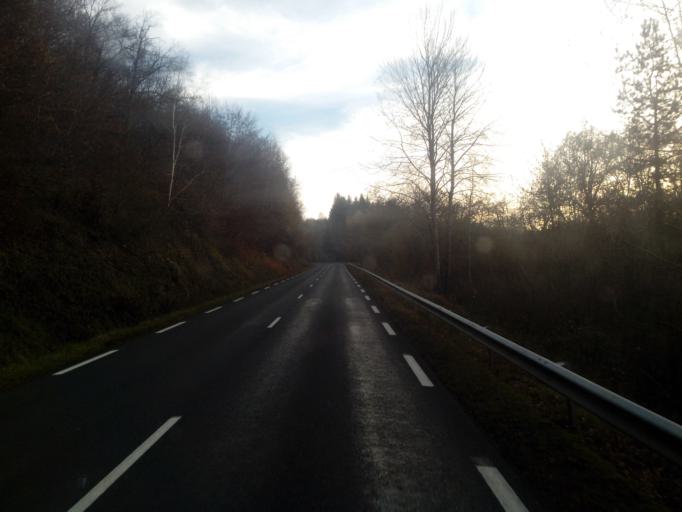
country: FR
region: Auvergne
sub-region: Departement du Cantal
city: Riom-es-Montagnes
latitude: 45.3227
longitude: 2.5999
